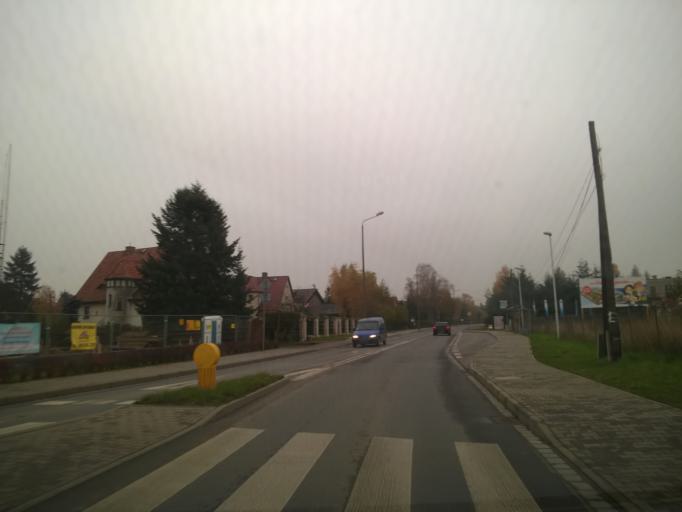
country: PL
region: Lower Silesian Voivodeship
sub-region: Powiat wroclawski
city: Zerniki Wroclawskie
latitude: 51.0619
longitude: 17.0323
